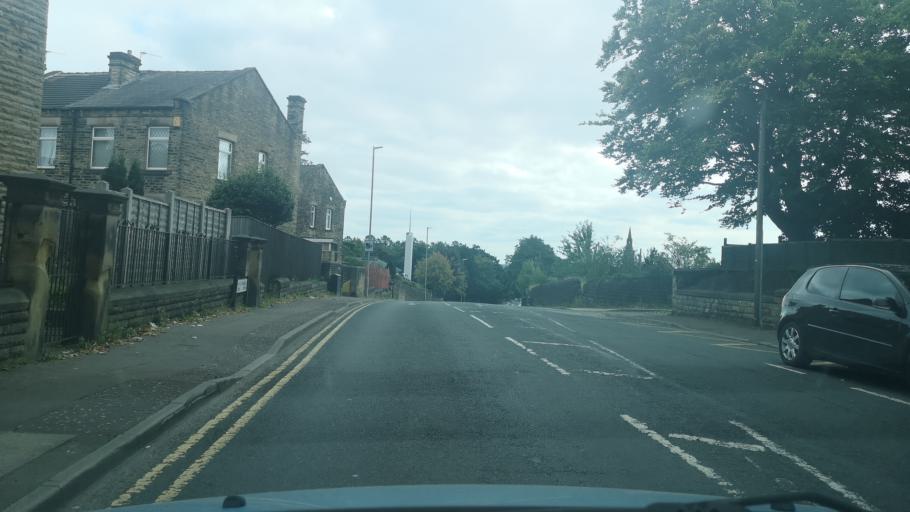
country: GB
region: England
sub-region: Kirklees
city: Batley
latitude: 53.7006
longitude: -1.6417
